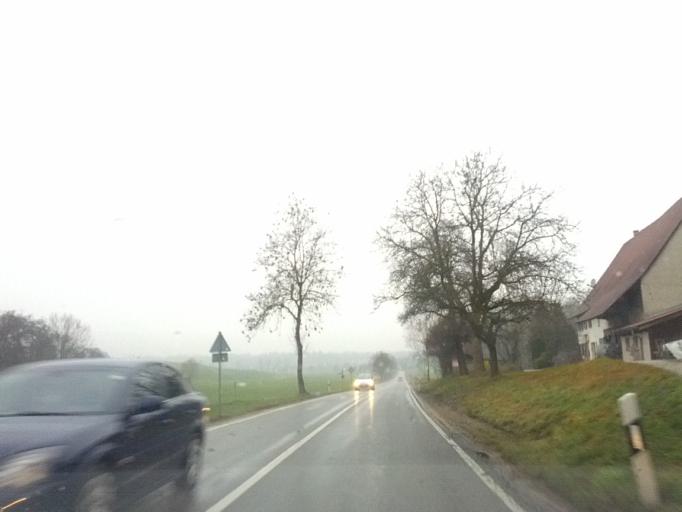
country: DE
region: Baden-Wuerttemberg
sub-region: Tuebingen Region
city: Ummendorf
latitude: 48.0733
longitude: 9.8432
